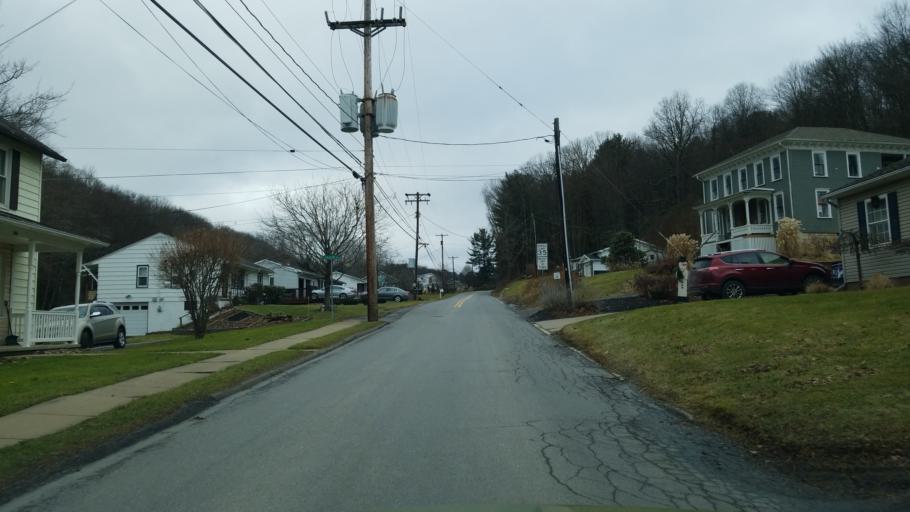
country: US
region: Pennsylvania
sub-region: Clearfield County
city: Clearfield
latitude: 41.0294
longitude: -78.4524
